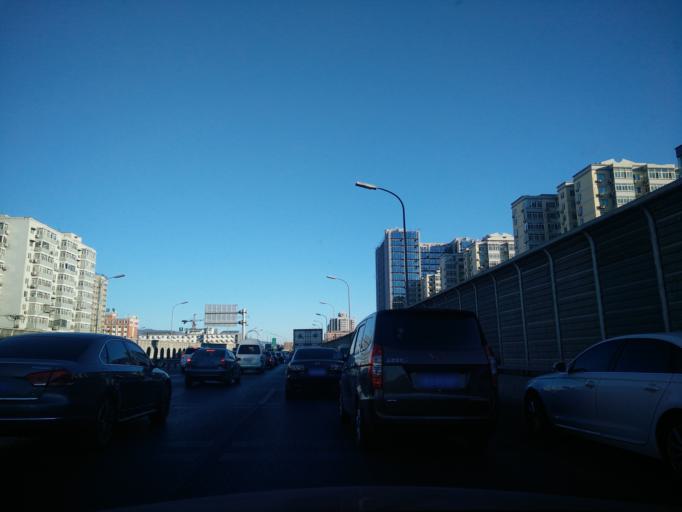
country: CN
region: Beijing
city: Lugu
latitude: 39.8988
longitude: 116.2052
